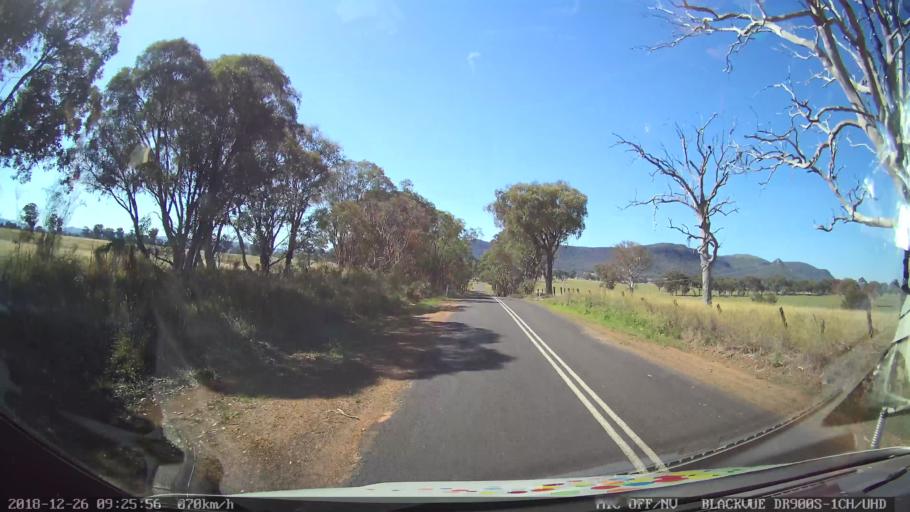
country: AU
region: New South Wales
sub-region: Mid-Western Regional
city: Kandos
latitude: -32.8247
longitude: 150.0058
